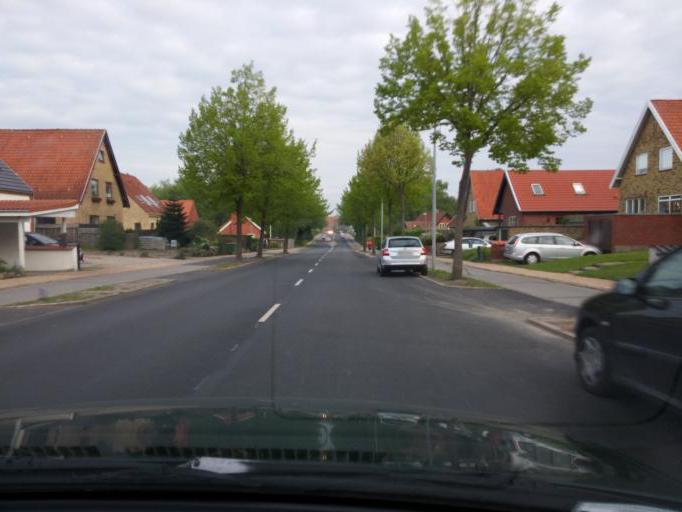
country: DK
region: South Denmark
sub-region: Odense Kommune
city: Odense
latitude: 55.3882
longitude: 10.4146
